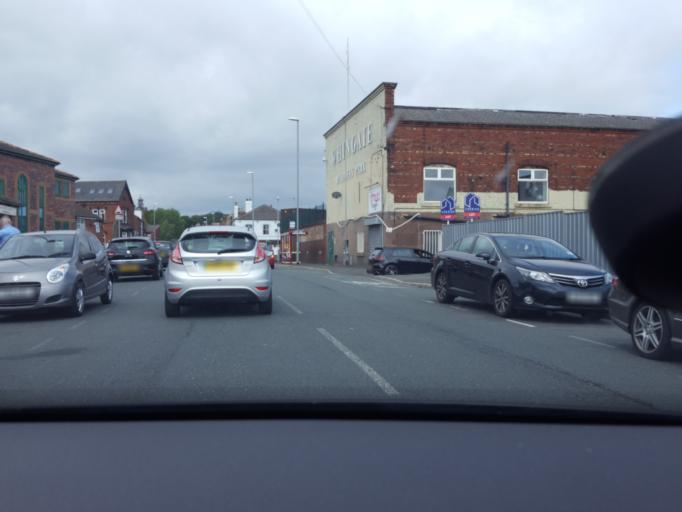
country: GB
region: England
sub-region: City and Borough of Leeds
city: Gildersome
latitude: 53.7947
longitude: -1.5990
